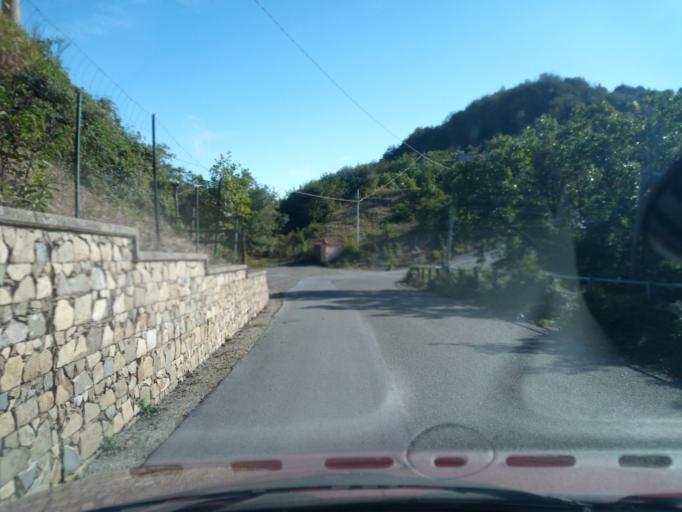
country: IT
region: Liguria
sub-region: Provincia di Genova
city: Campomorone
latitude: 44.4905
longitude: 8.8543
